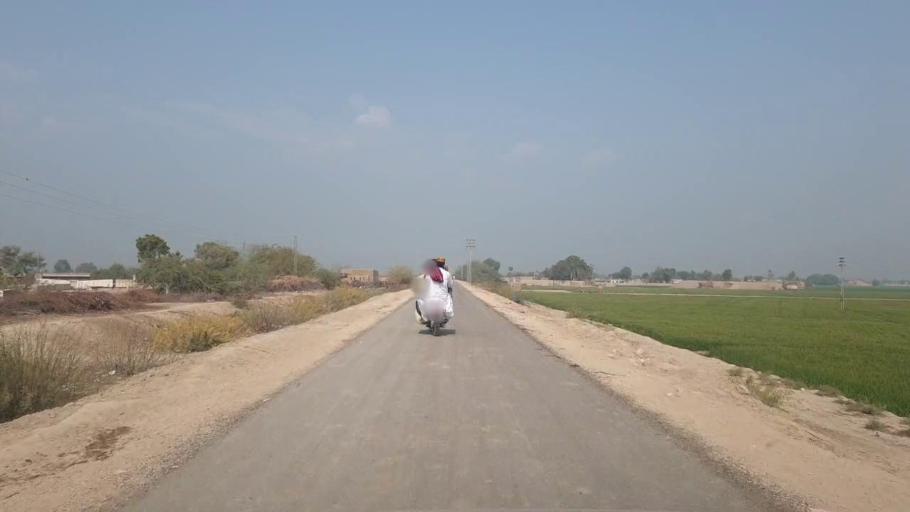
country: PK
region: Sindh
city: Hala
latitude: 25.7977
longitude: 68.4011
